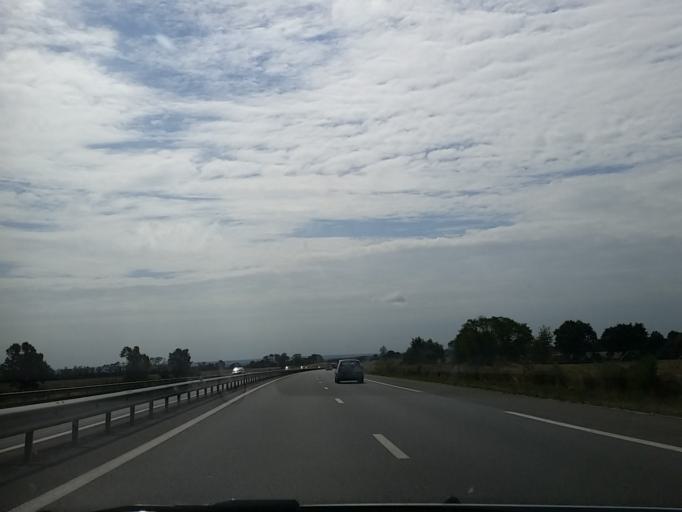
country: FR
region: Auvergne
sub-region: Departement de l'Allier
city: Vallon-en-Sully
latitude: 46.5867
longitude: 2.5215
